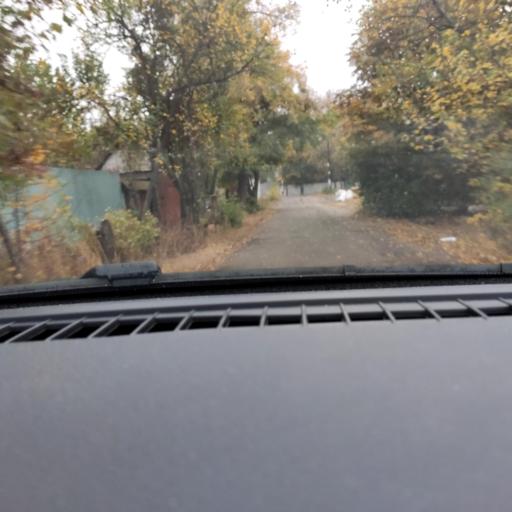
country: RU
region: Voronezj
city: Voronezh
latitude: 51.6944
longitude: 39.2161
